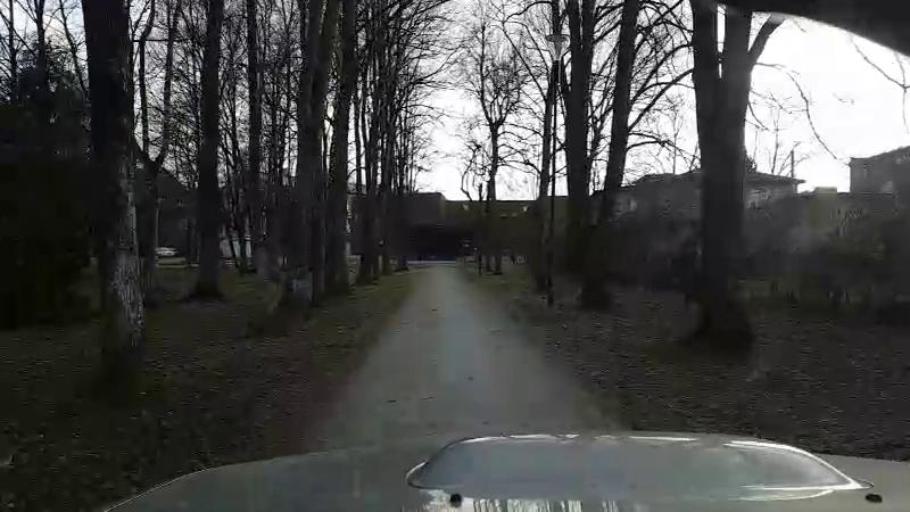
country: EE
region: Jaervamaa
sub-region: Paide linn
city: Paide
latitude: 58.8883
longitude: 25.5614
